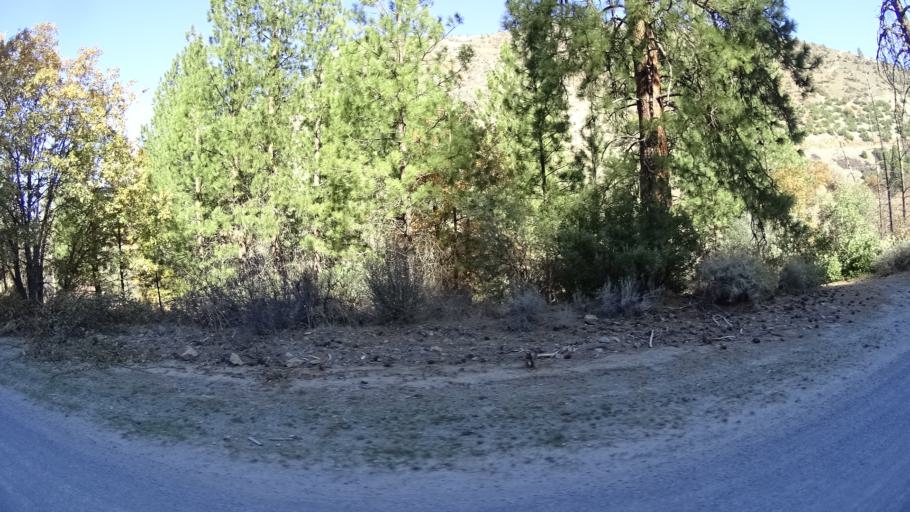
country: US
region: California
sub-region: Siskiyou County
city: Yreka
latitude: 41.8325
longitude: -122.6629
